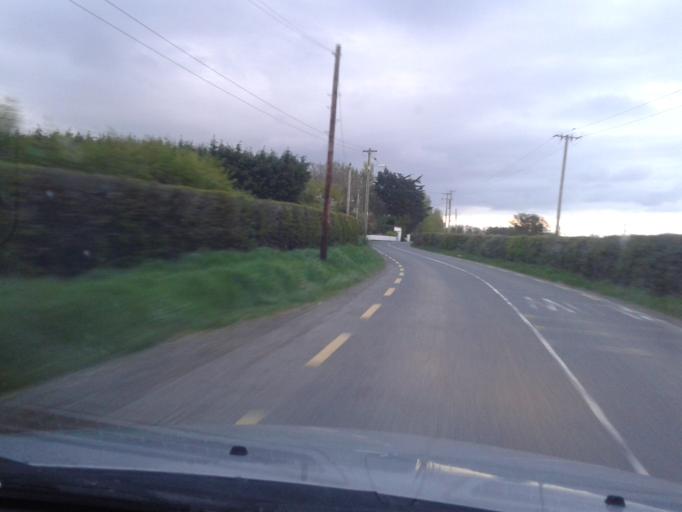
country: IE
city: Bonnybrook
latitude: 53.4133
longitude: -6.2141
